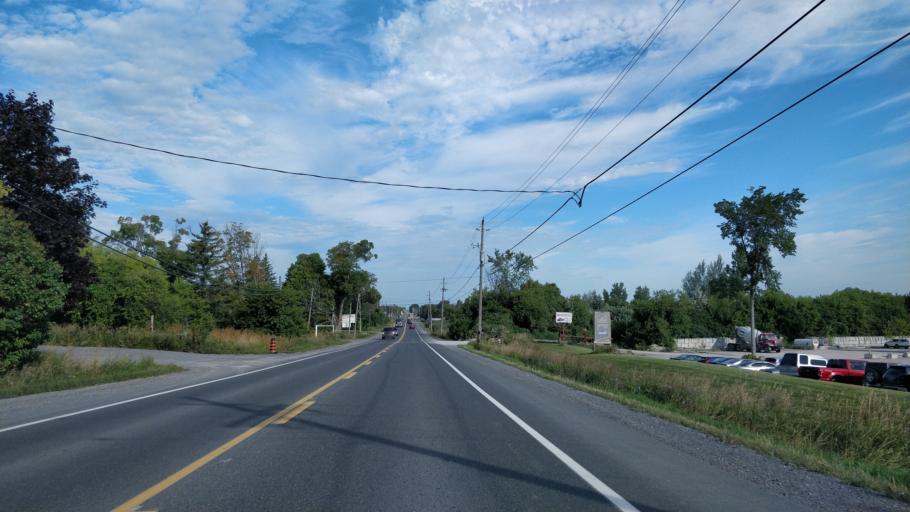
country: CA
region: Ontario
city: Bells Corners
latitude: 45.2881
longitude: -75.9658
